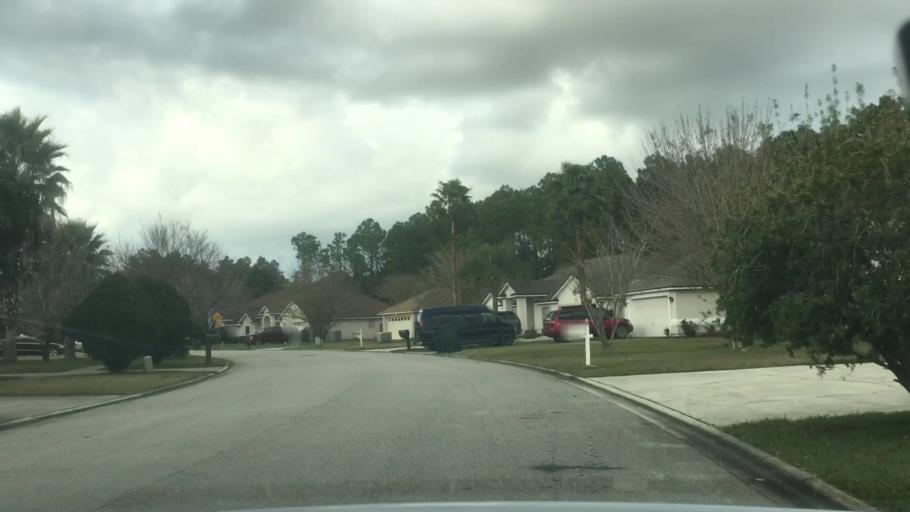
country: US
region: Florida
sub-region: Duval County
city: Atlantic Beach
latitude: 30.3182
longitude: -81.5066
